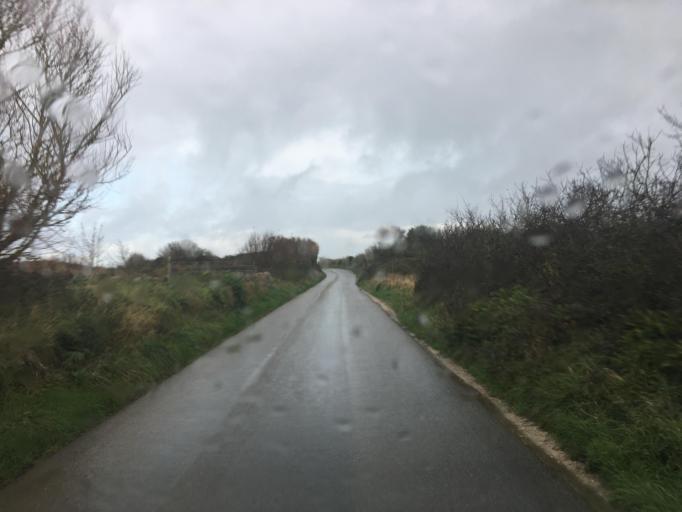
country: FR
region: Lower Normandy
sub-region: Departement de la Manche
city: Reville
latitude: 49.6901
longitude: -1.2783
